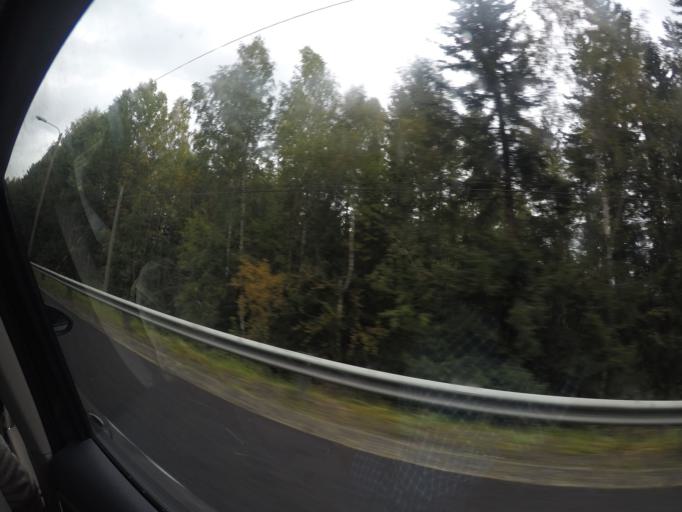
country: FI
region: Pirkanmaa
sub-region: Tampere
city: Kangasala
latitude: 61.4452
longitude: 24.1117
